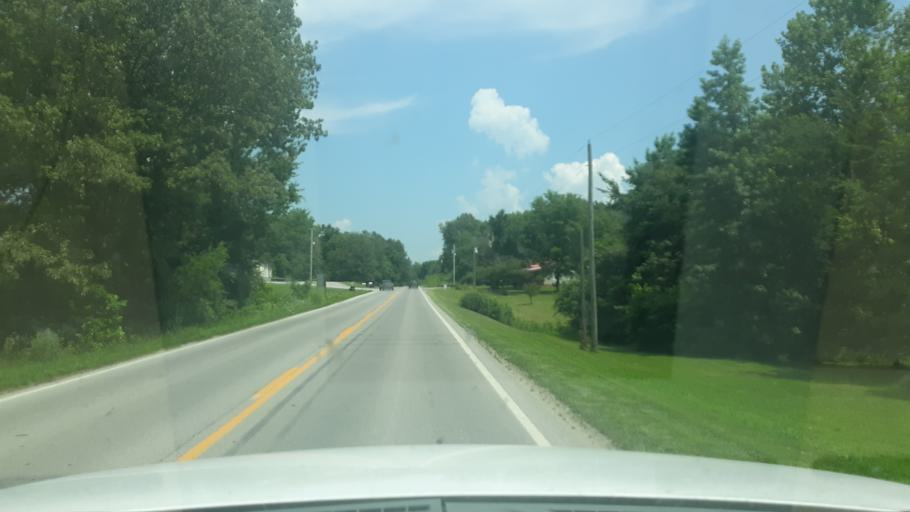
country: US
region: Illinois
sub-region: Saline County
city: Harrisburg
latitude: 37.8378
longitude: -88.5962
